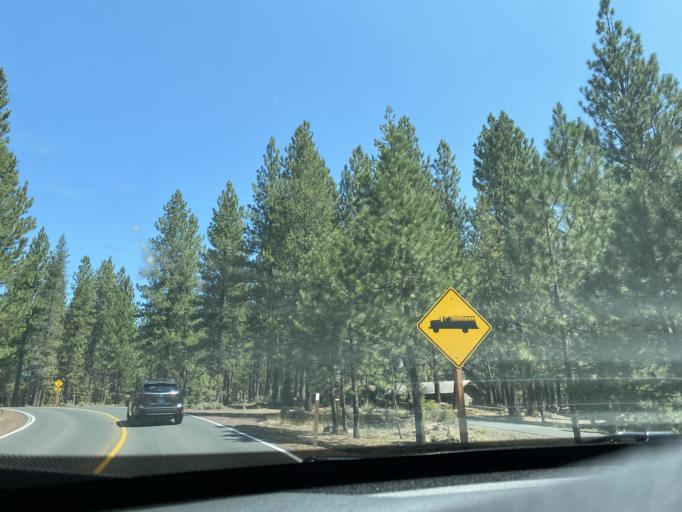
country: US
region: Oregon
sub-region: Deschutes County
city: Sunriver
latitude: 43.8861
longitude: -121.4389
